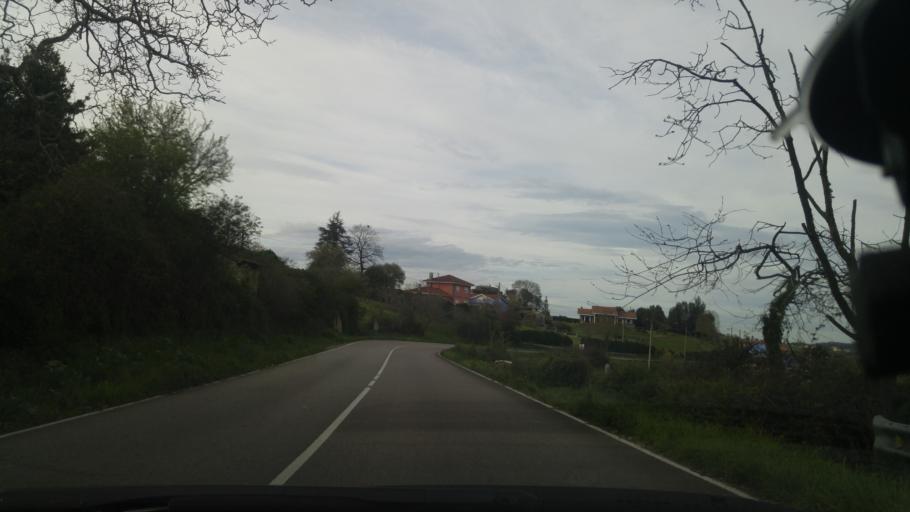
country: ES
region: Asturias
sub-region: Province of Asturias
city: Corvera de Asturias
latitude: 43.4730
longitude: -5.8461
